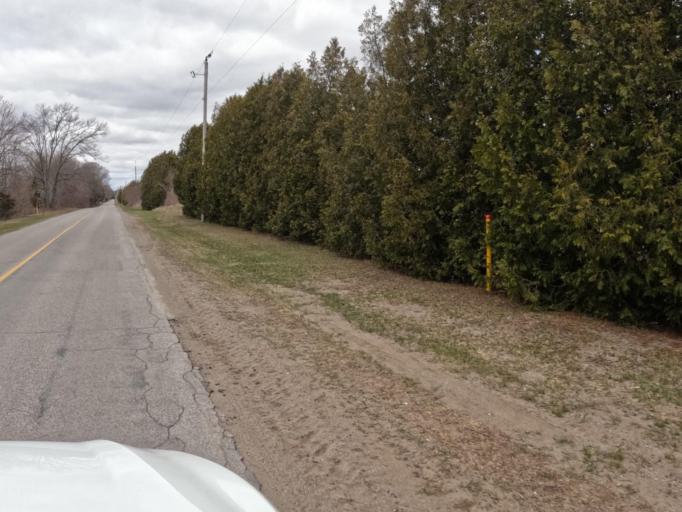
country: CA
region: Ontario
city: Norfolk County
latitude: 42.8027
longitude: -80.3663
